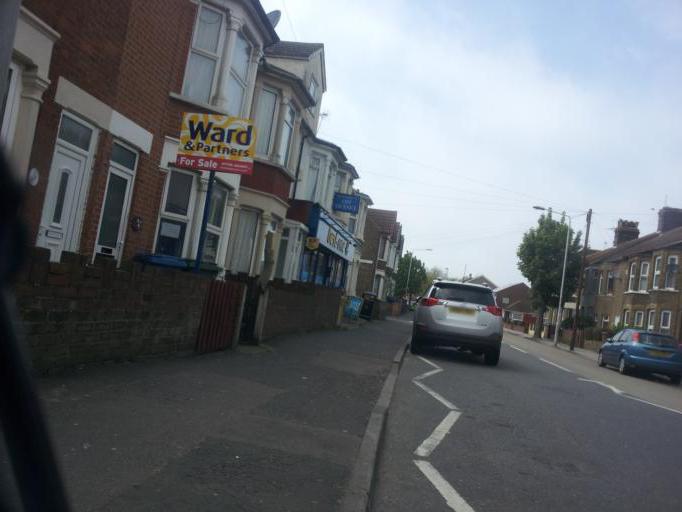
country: GB
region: England
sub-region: Kent
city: Queenborough
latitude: 51.4150
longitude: 0.7525
